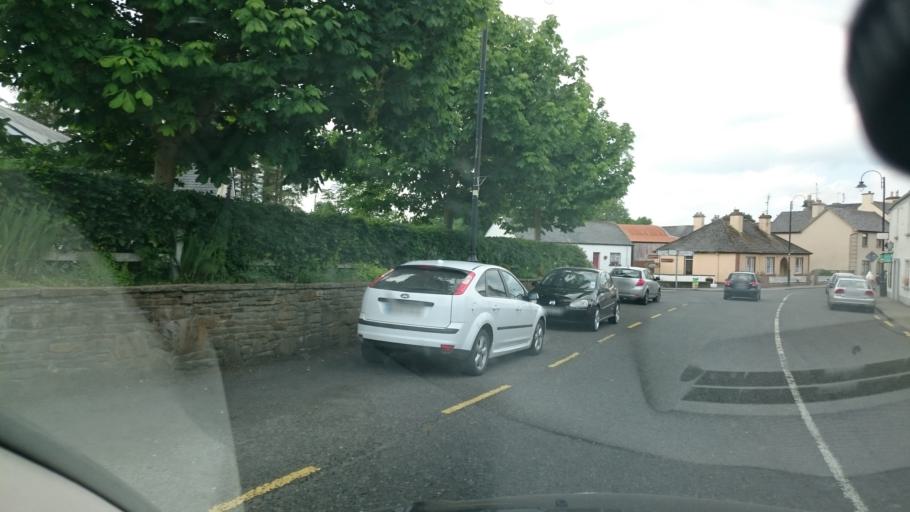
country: IE
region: Connaught
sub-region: Sligo
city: Inishcrone
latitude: 54.1100
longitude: -9.0236
